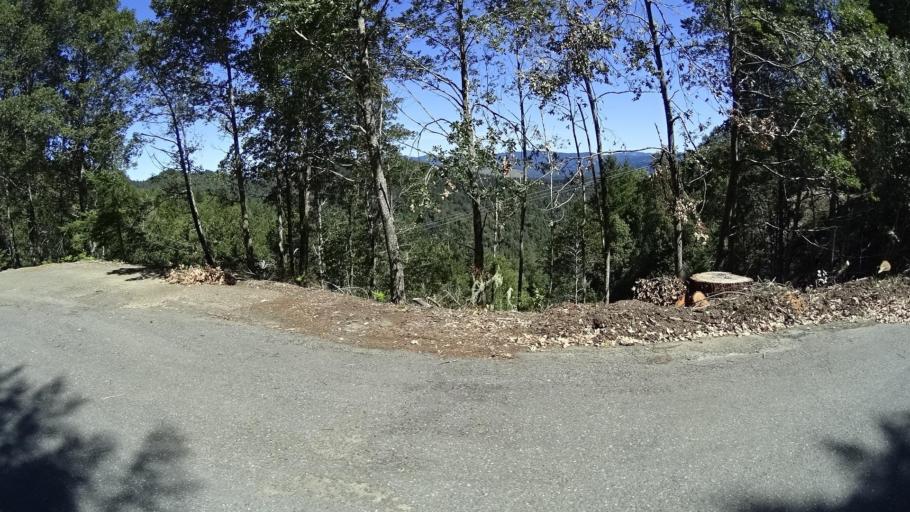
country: US
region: California
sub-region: Humboldt County
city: Redway
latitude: 40.1506
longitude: -124.0611
